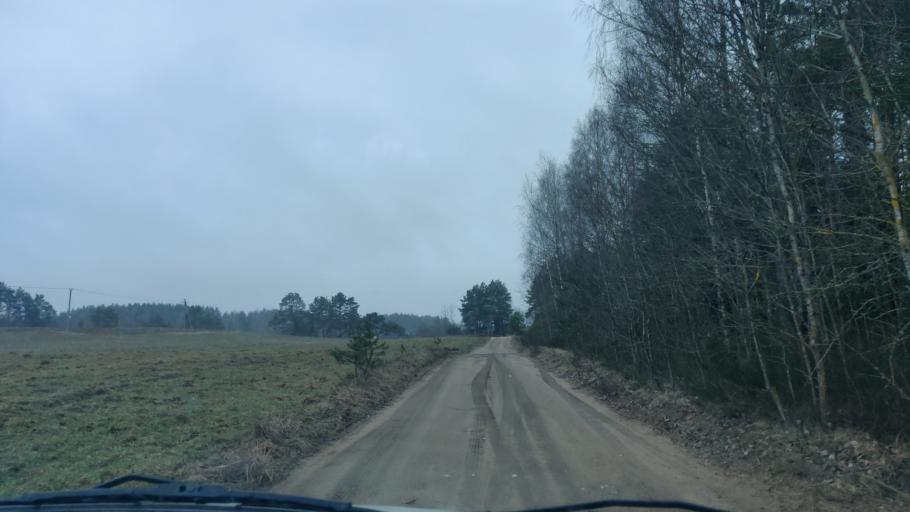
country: LT
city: Trakai
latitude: 54.5525
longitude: 24.9491
